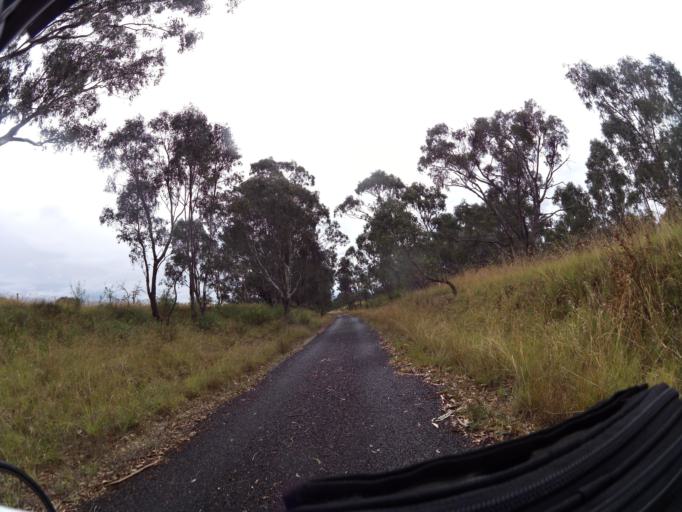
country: AU
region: New South Wales
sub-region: Albury Municipality
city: East Albury
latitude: -36.1404
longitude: 146.9924
